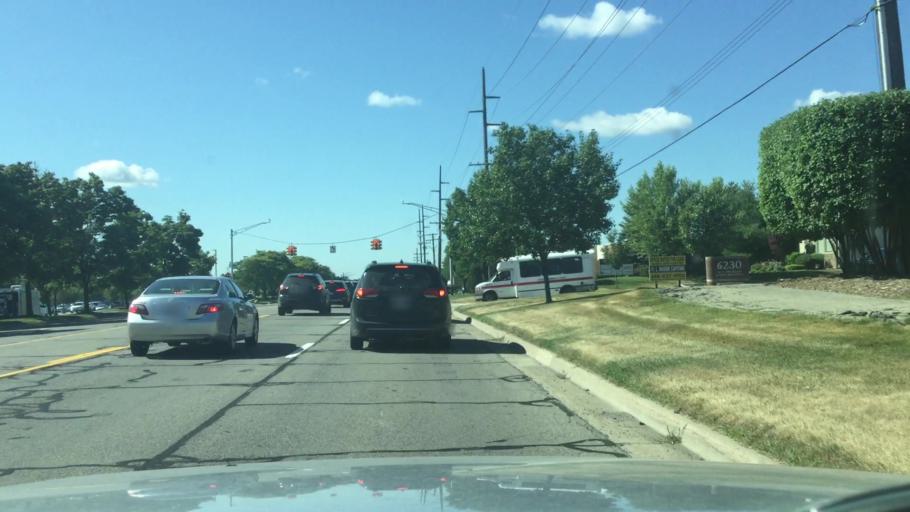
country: US
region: Michigan
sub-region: Oakland County
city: West Bloomfield Township
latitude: 42.5471
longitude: -83.3610
